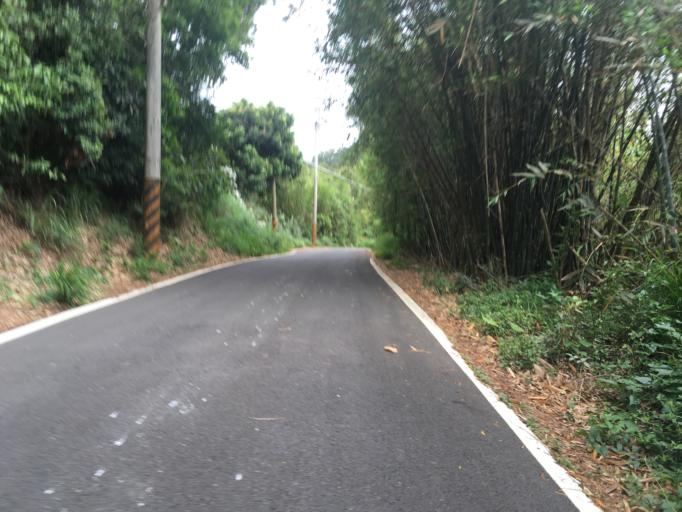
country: TW
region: Taiwan
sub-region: Hsinchu
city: Hsinchu
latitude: 24.7461
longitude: 120.9845
